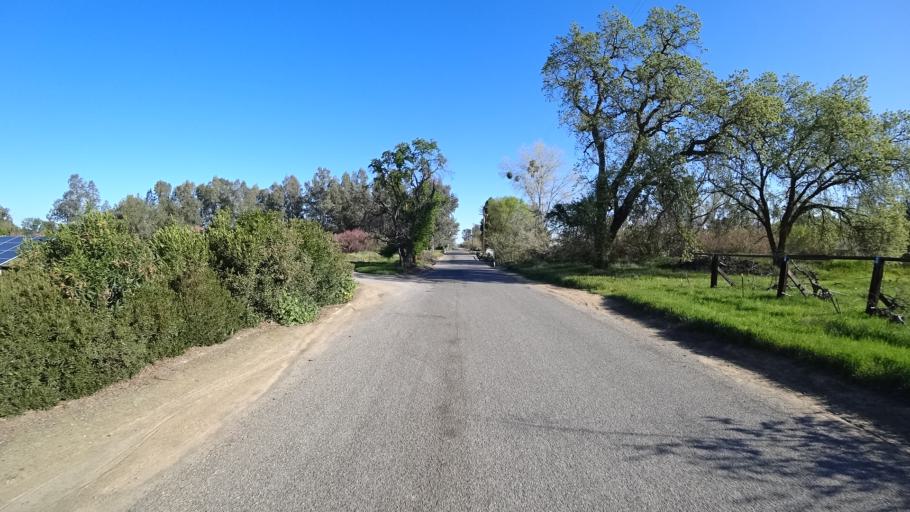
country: US
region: California
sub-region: Glenn County
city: Orland
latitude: 39.7667
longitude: -122.2202
